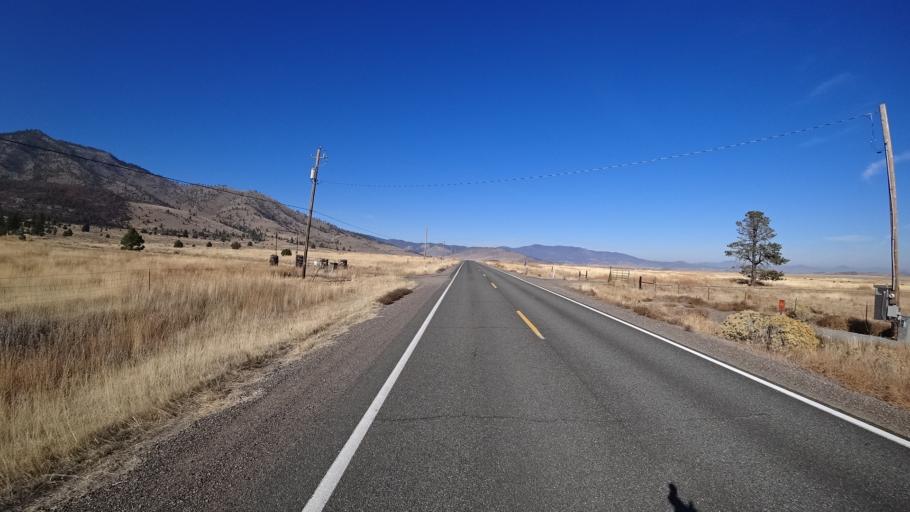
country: US
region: California
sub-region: Siskiyou County
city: Weed
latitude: 41.4750
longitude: -122.4859
